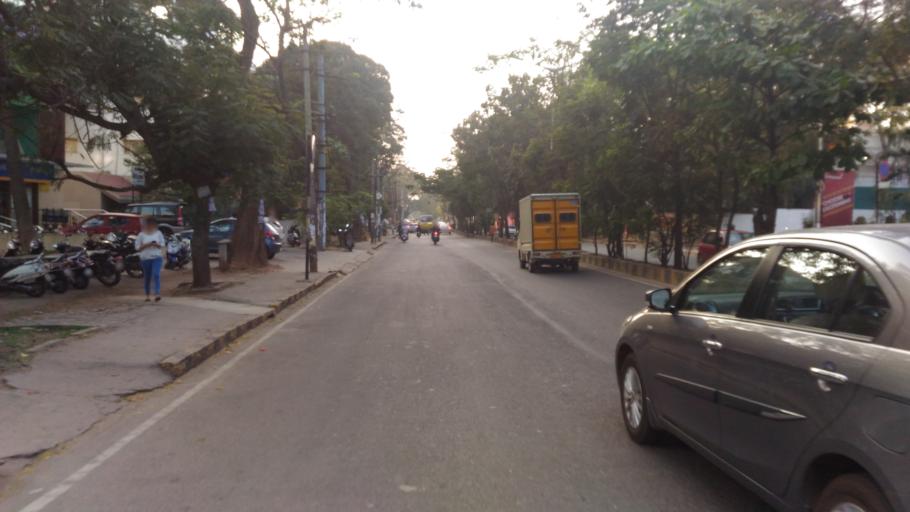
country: IN
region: Karnataka
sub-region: Bangalore Urban
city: Bangalore
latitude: 12.9064
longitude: 77.5798
